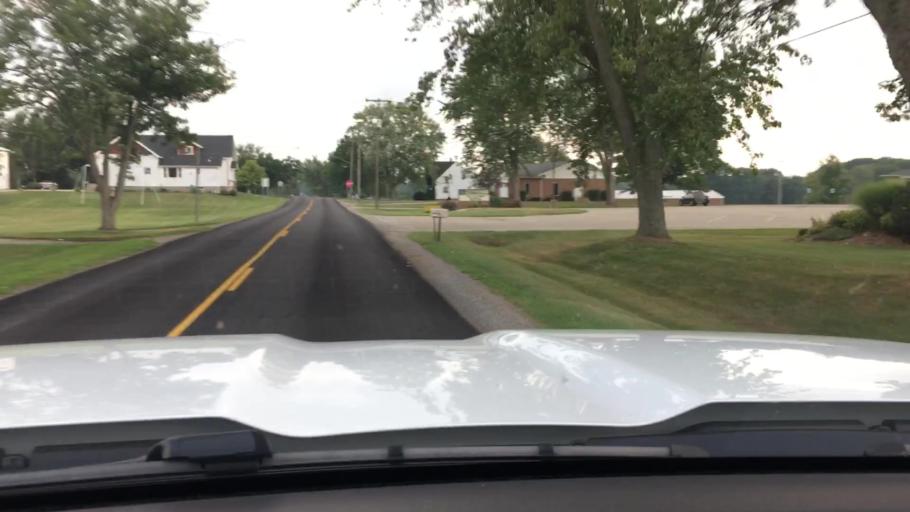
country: US
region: Michigan
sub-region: Ottawa County
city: Hudsonville
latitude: 42.8273
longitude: -85.8817
